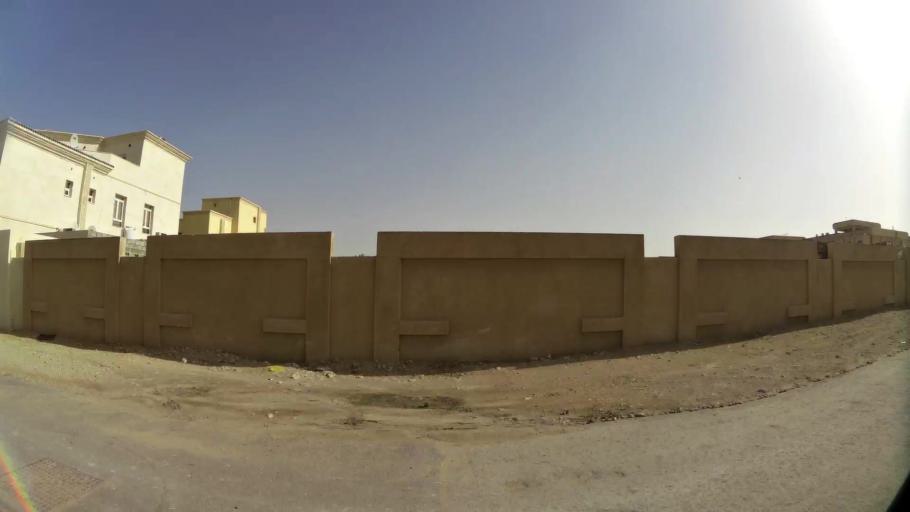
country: QA
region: Baladiyat ar Rayyan
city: Ar Rayyan
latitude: 25.3280
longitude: 51.4221
